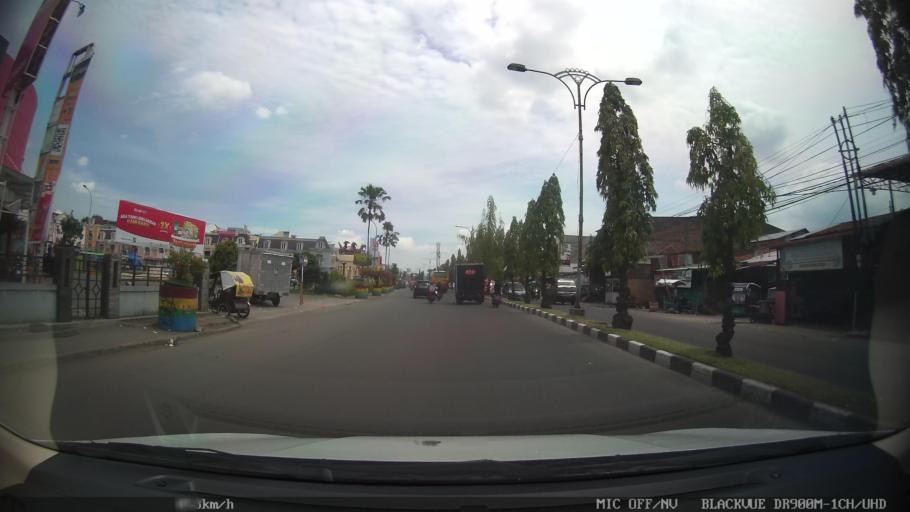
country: ID
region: North Sumatra
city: Medan
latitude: 3.5472
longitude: 98.6595
